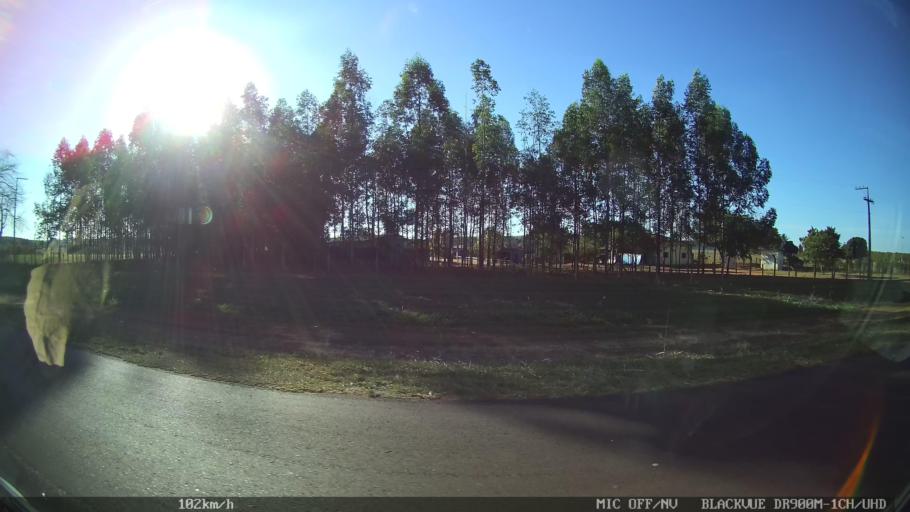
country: BR
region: Sao Paulo
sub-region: Guapiacu
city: Guapiacu
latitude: -20.7495
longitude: -49.1314
